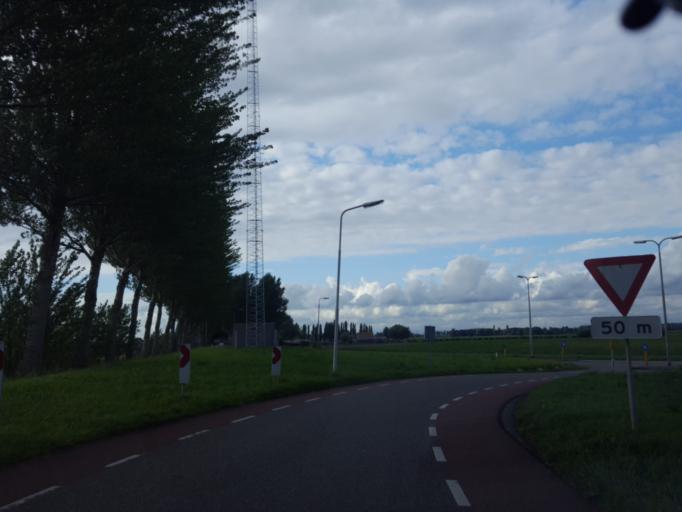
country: NL
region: South Holland
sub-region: Gemeente Spijkenisse
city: Spijkenisse
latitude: 51.7633
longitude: 4.3358
